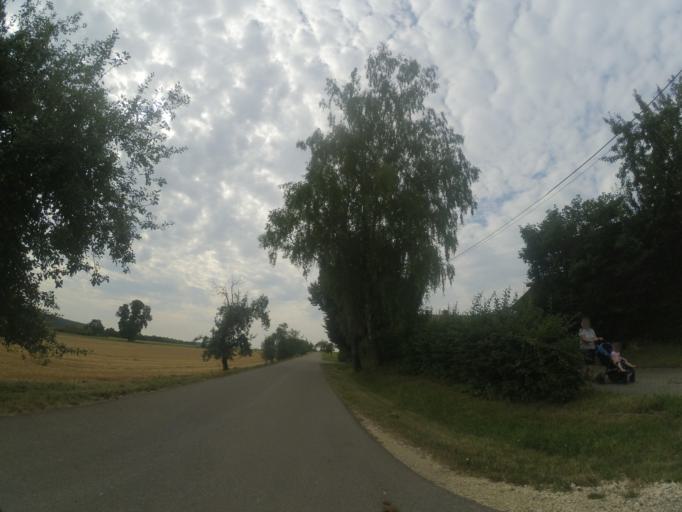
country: DE
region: Baden-Wuerttemberg
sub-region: Tuebingen Region
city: Westerstetten
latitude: 48.5186
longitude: 9.9460
